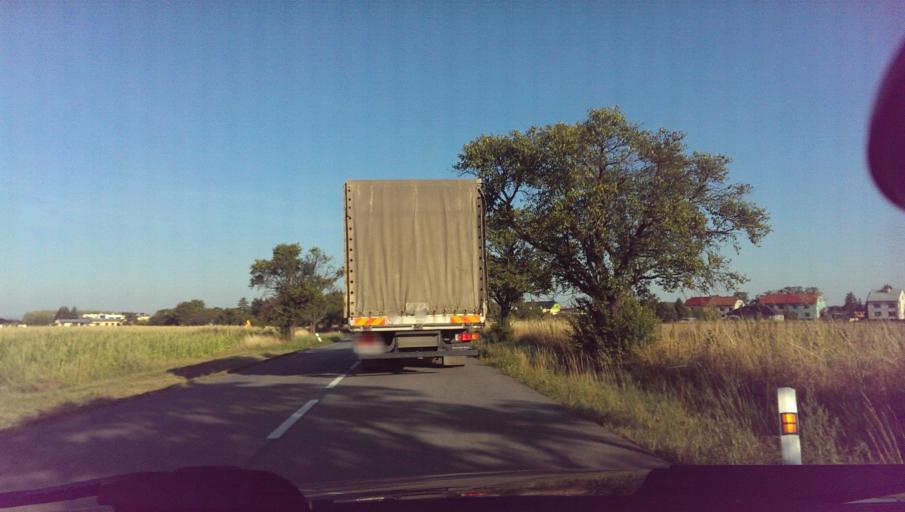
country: CZ
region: Zlin
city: Holesov
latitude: 49.3071
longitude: 17.6105
